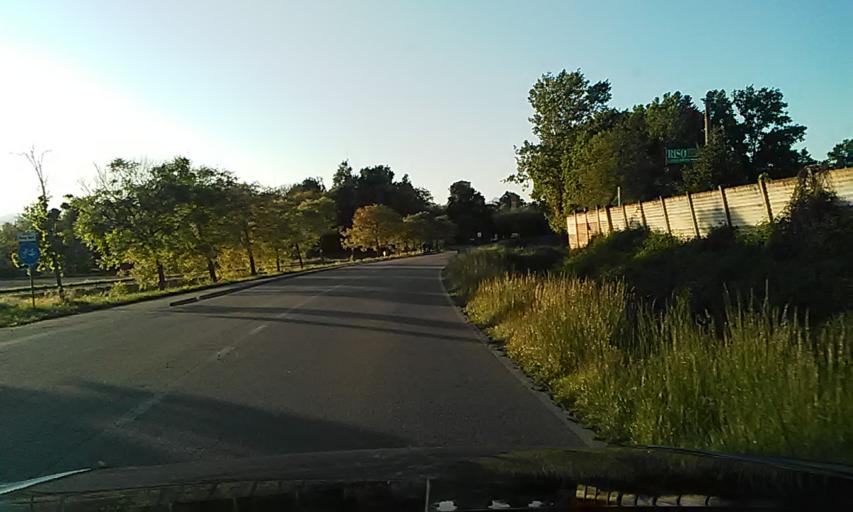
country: IT
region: Piedmont
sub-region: Provincia di Vercelli
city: Rovasenda
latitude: 45.5310
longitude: 8.3157
